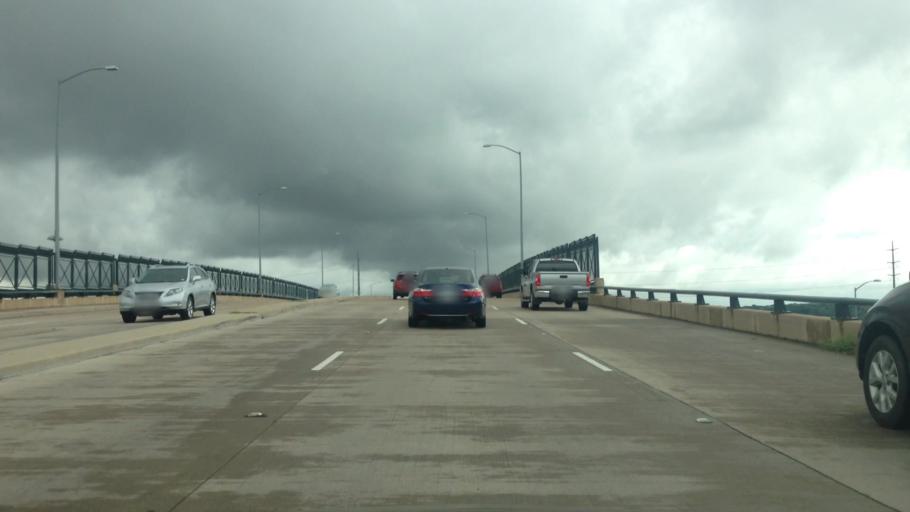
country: US
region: Texas
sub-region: Tarrant County
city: Westworth
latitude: 32.7204
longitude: -97.3866
